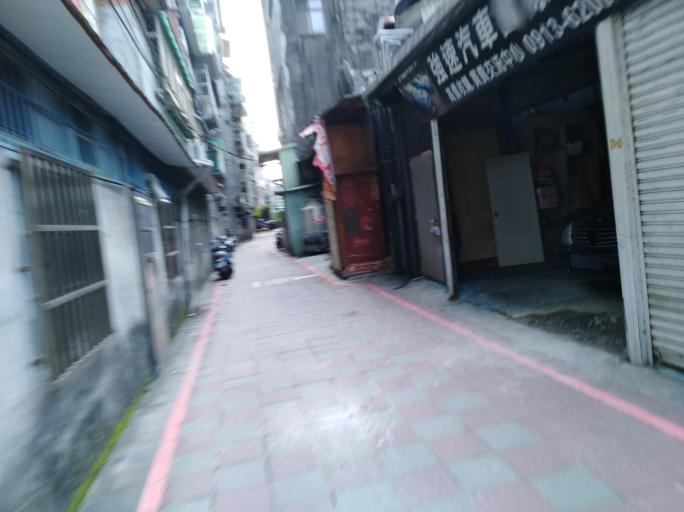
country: TW
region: Taipei
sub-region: Taipei
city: Banqiao
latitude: 25.0390
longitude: 121.4249
